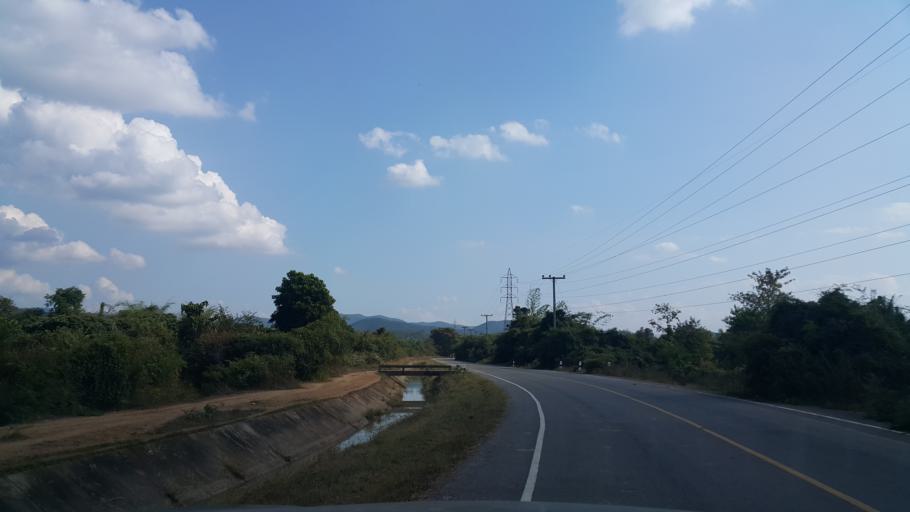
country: TH
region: Lamphun
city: Mae Tha
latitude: 18.5360
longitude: 99.0956
